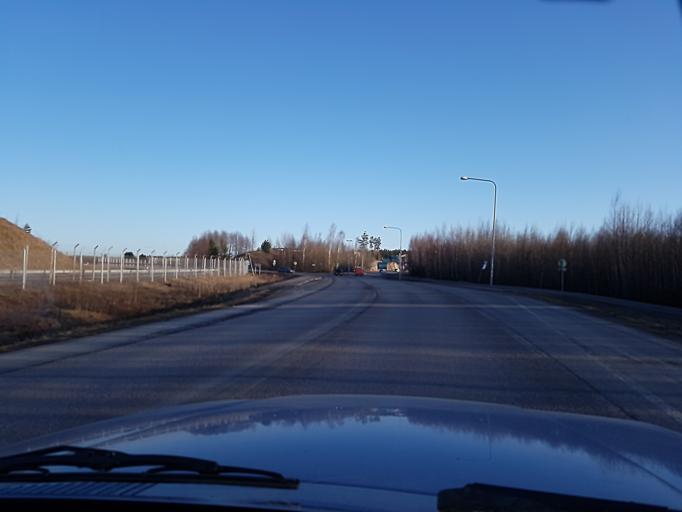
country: FI
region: Uusimaa
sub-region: Helsinki
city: Vantaa
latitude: 60.3053
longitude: 24.9935
